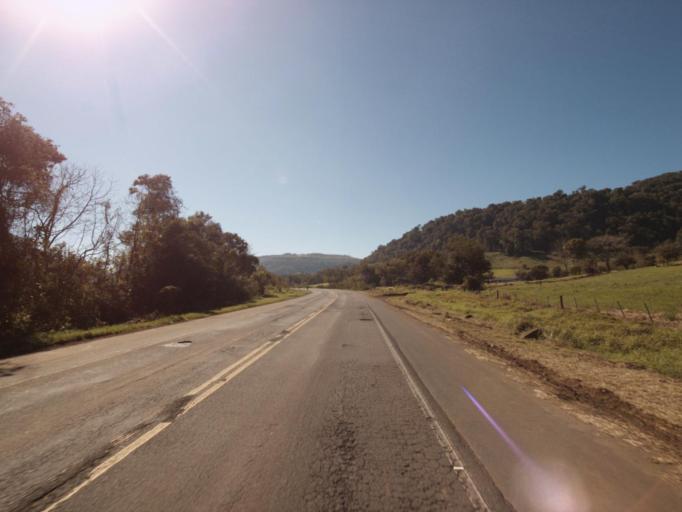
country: BR
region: Rio Grande do Sul
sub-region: Frederico Westphalen
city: Frederico Westphalen
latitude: -26.9848
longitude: -53.2239
